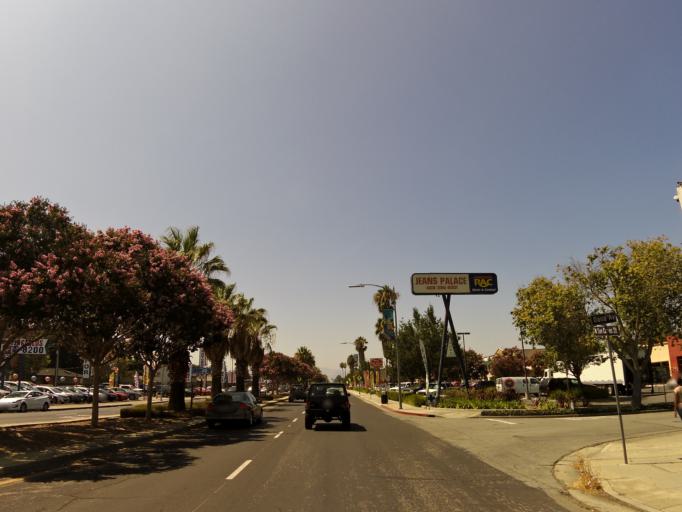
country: US
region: California
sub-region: Santa Clara County
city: Buena Vista
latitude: 37.3235
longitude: -121.9197
